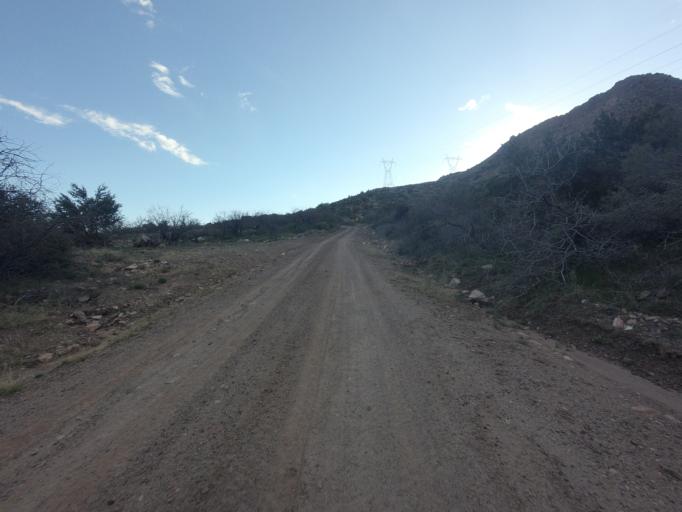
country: US
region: Arizona
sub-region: Gila County
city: Pine
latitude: 34.3703
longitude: -111.6693
